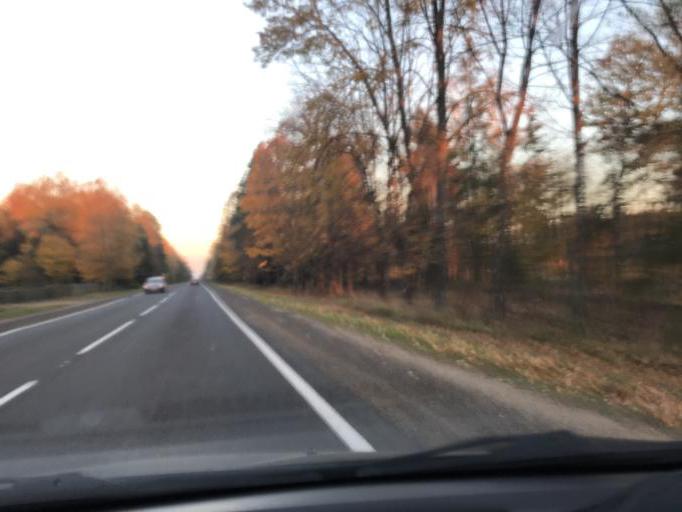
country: BY
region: Mogilev
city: Hlusha
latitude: 53.0883
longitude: 28.8712
